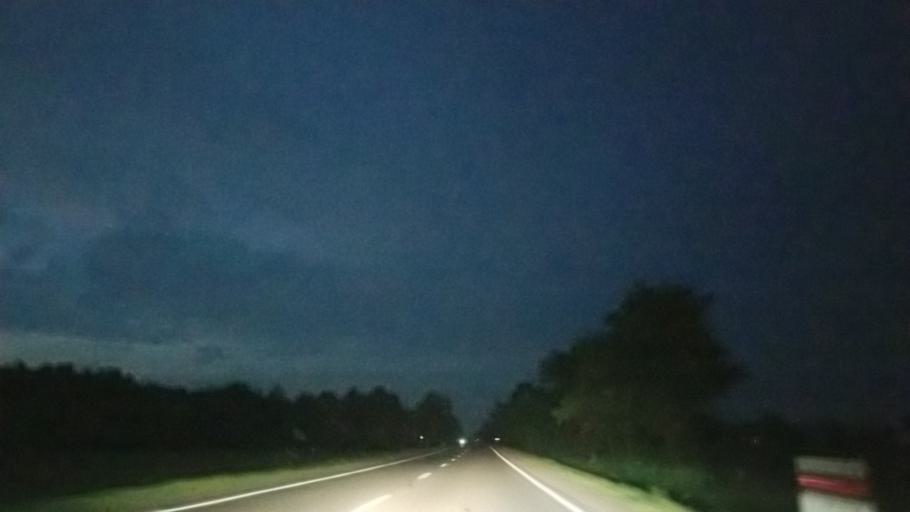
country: PL
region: Lublin Voivodeship
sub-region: Powiat bialski
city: Koden
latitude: 51.9762
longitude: 23.6951
